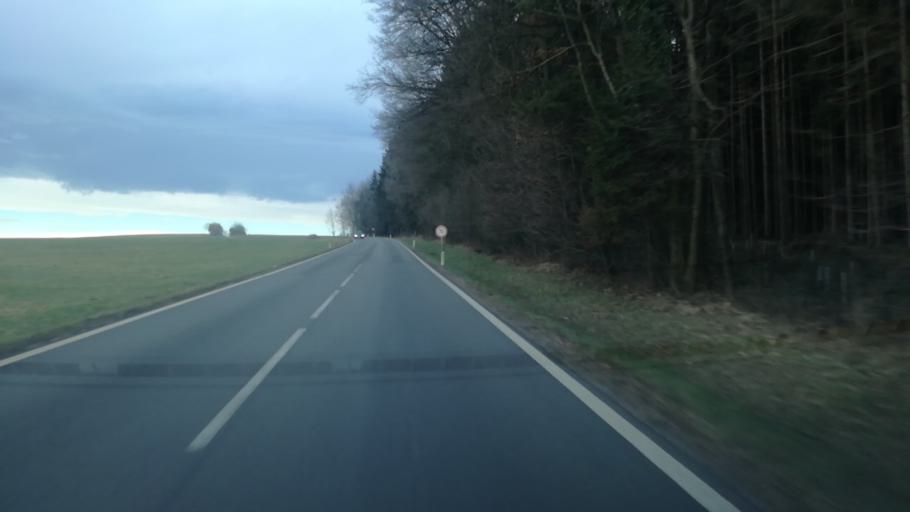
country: AT
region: Upper Austria
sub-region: Politischer Bezirk Ried im Innkreis
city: Waldzell
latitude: 48.1677
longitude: 13.4415
